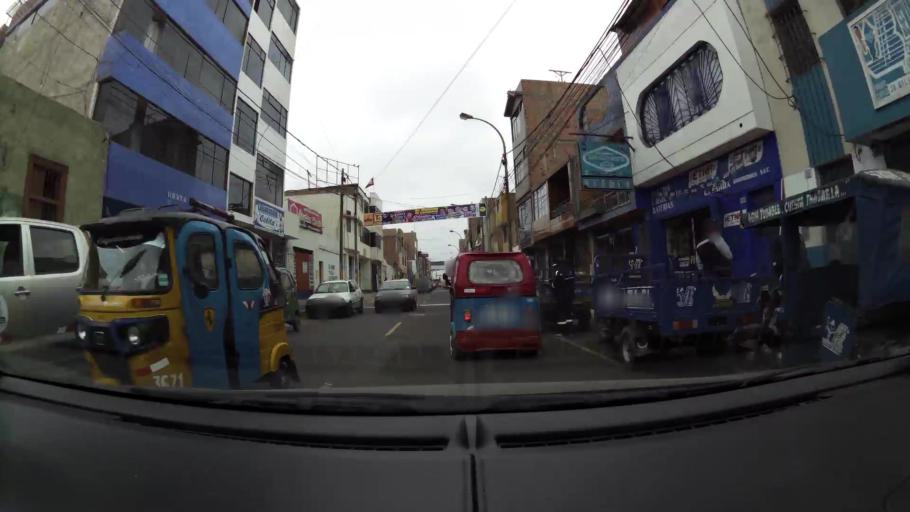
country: PE
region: Lima
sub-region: Barranca
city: Barranca
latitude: -10.7550
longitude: -77.7577
